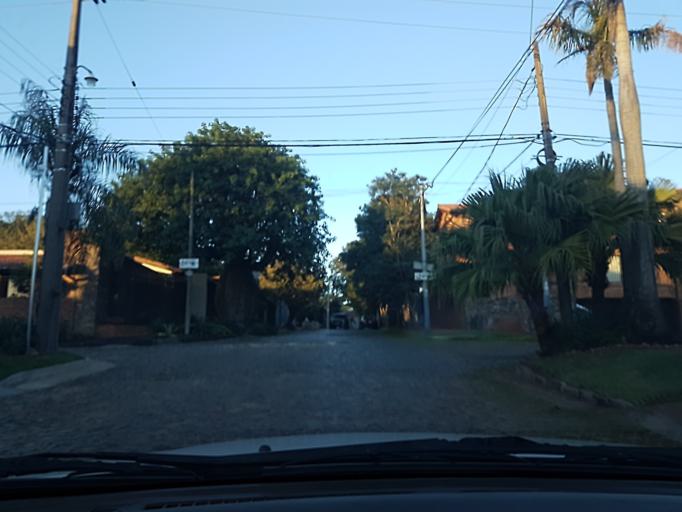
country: PY
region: Asuncion
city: Asuncion
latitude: -25.2709
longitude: -57.5692
